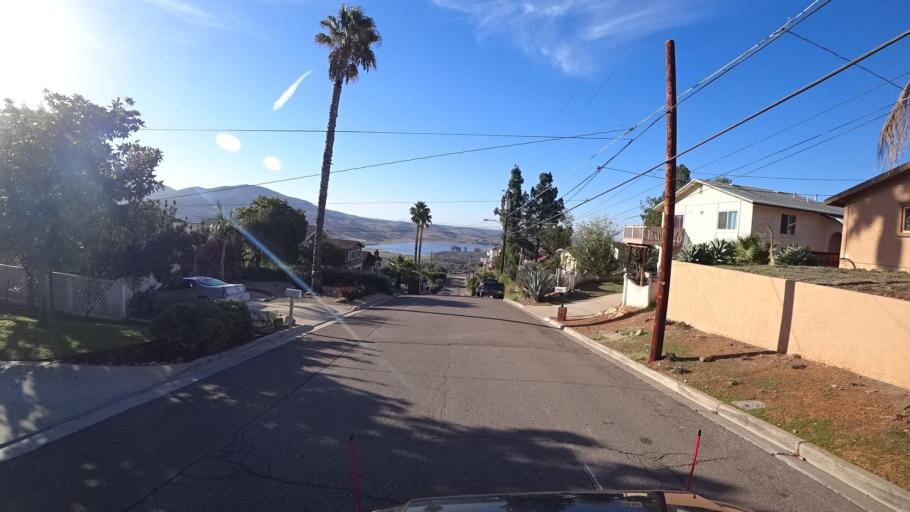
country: US
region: California
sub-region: San Diego County
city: La Presa
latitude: 32.7165
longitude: -116.9854
